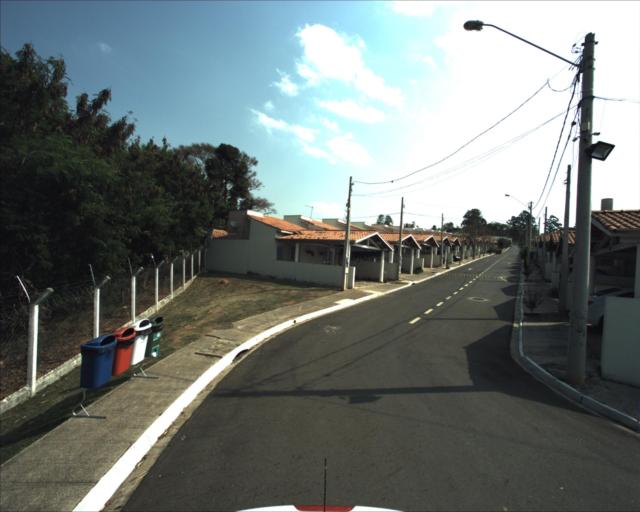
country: BR
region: Sao Paulo
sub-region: Sorocaba
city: Sorocaba
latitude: -23.4521
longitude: -47.4940
